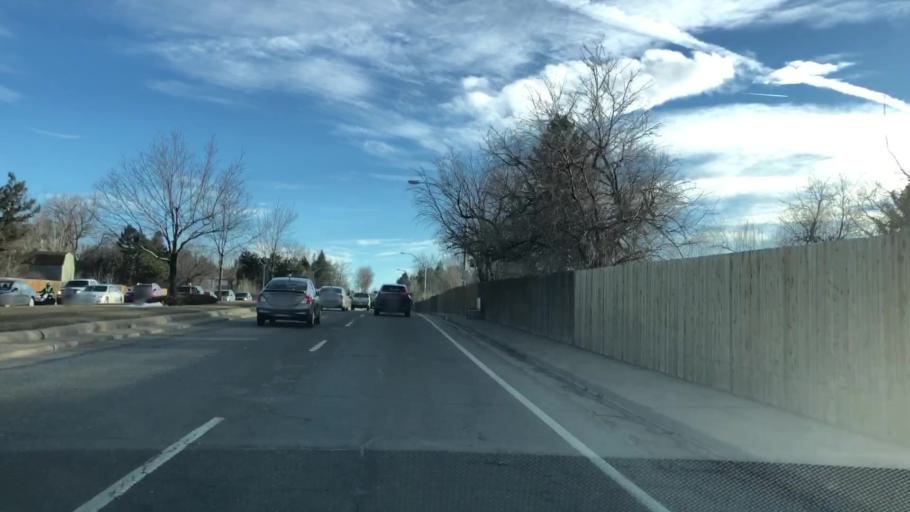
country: US
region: Colorado
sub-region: Adams County
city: Aurora
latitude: 39.6602
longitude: -104.7914
